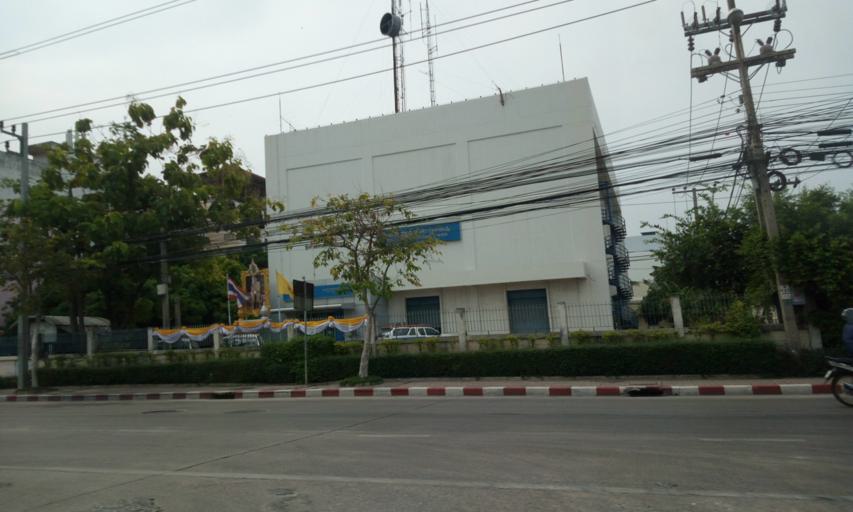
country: TH
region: Bangkok
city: Lat Krabang
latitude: 13.7217
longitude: 100.7638
